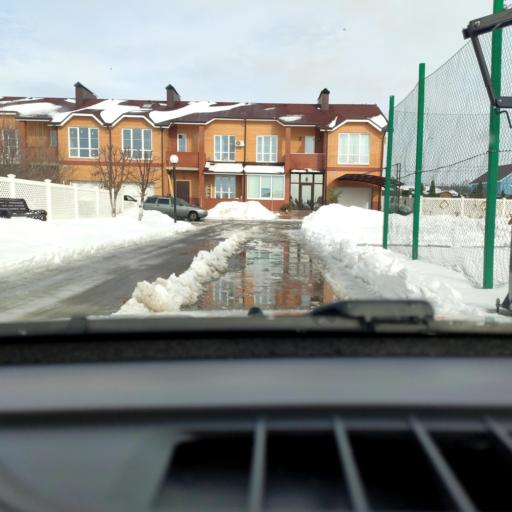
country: RU
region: Voronezj
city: Podgornoye
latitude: 51.7705
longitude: 39.1268
